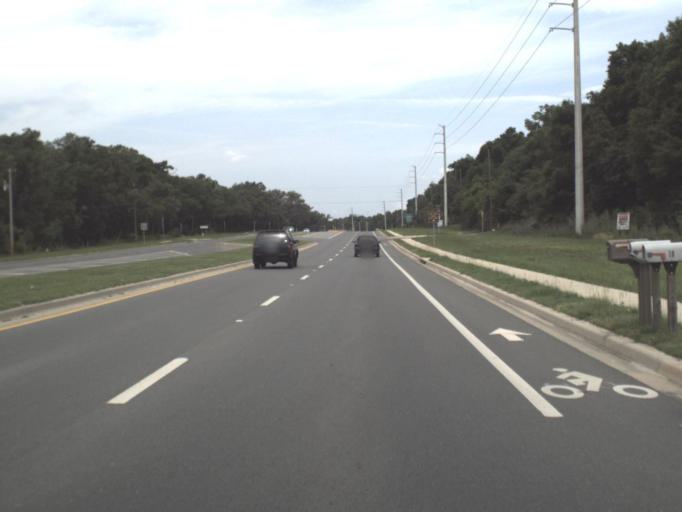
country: US
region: Florida
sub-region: Putnam County
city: Interlachen
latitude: 29.6283
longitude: -81.8687
